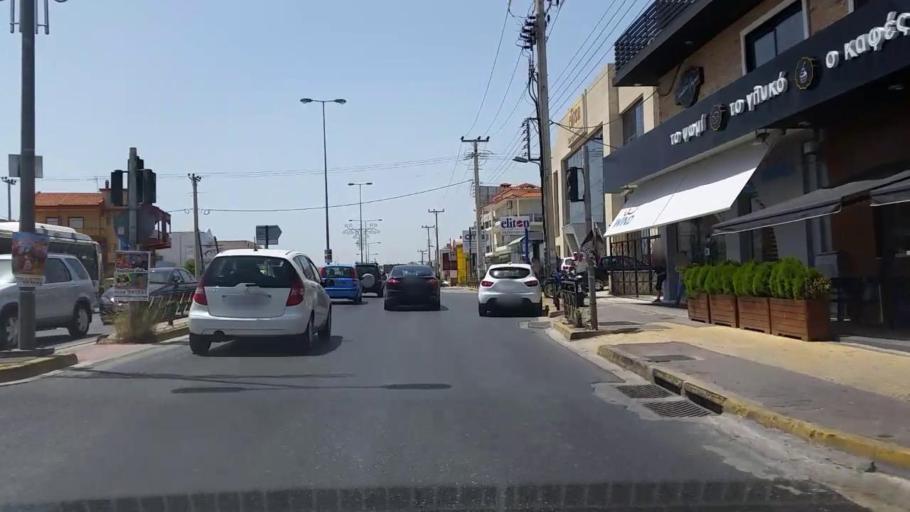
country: GR
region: Attica
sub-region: Nomarchia Anatolikis Attikis
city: Gerakas
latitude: 38.0084
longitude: 23.8560
